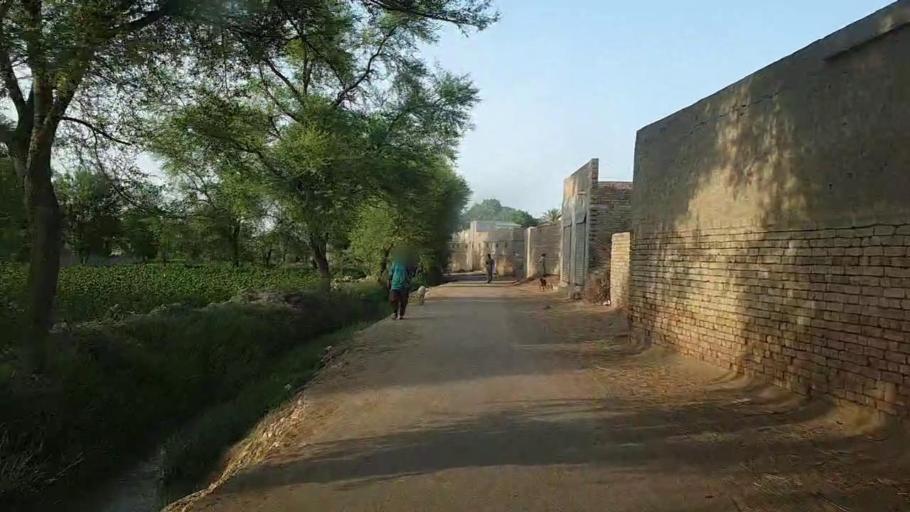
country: PK
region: Sindh
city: Ubauro
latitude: 28.1340
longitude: 69.8356
